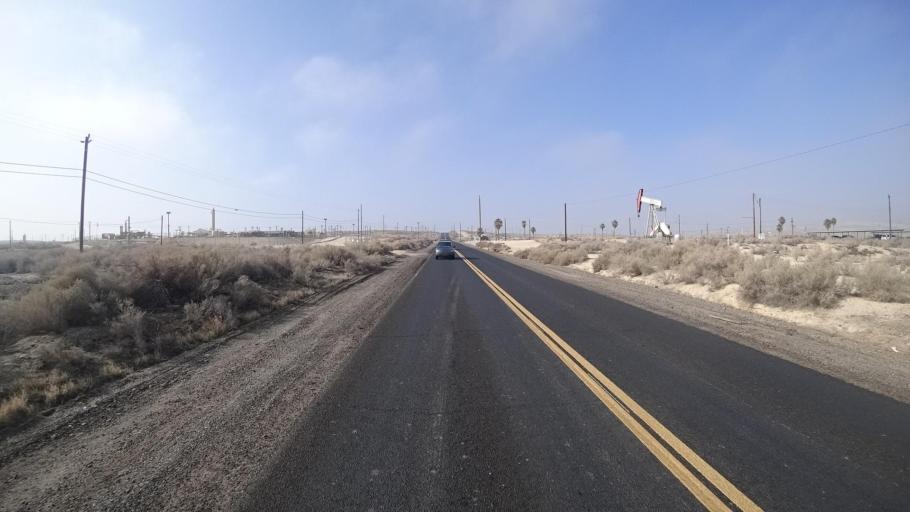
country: US
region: California
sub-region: Kern County
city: Ford City
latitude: 35.1806
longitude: -119.4591
